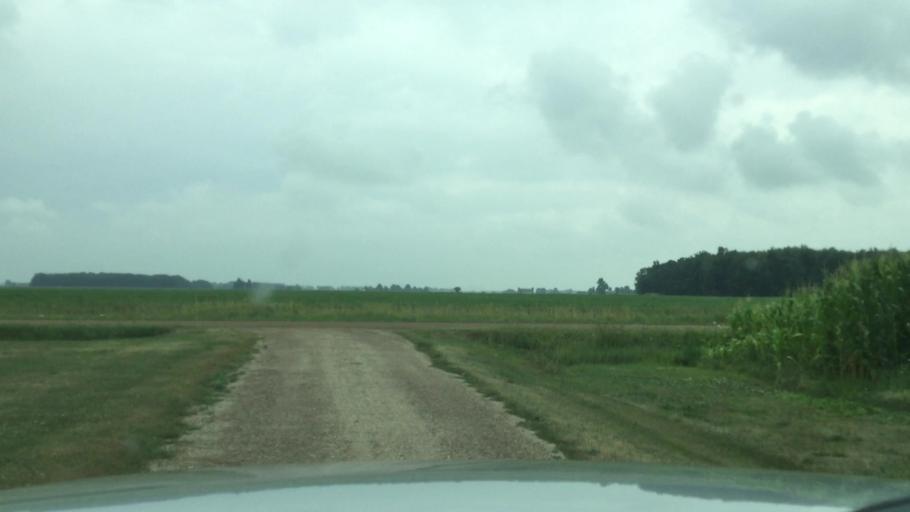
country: US
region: Michigan
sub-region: Shiawassee County
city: New Haven
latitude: 43.1158
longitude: -84.2334
